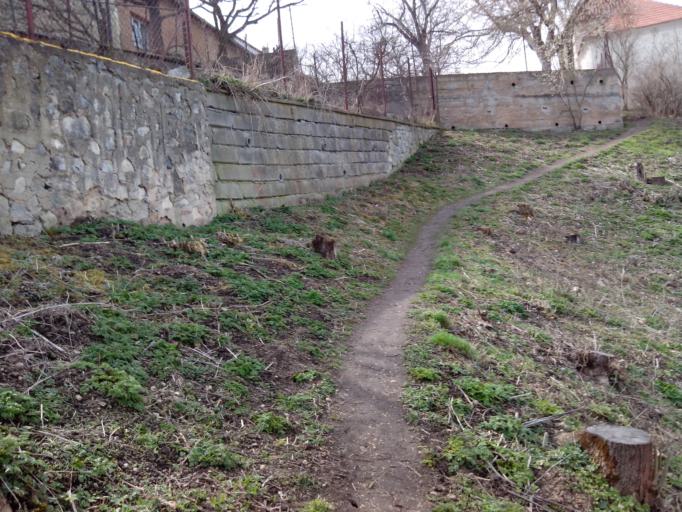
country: CZ
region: Central Bohemia
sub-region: Okres Beroun
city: Beroun
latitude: 49.9500
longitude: 14.1048
